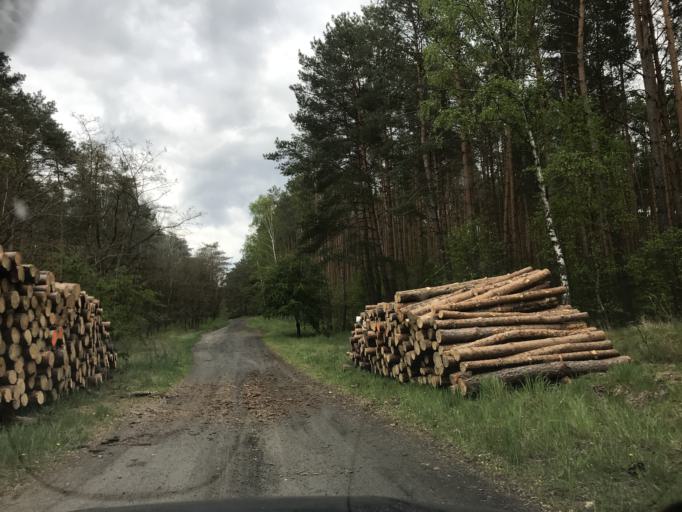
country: PL
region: West Pomeranian Voivodeship
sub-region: Powiat mysliborski
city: Mysliborz
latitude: 52.8709
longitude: 14.8791
